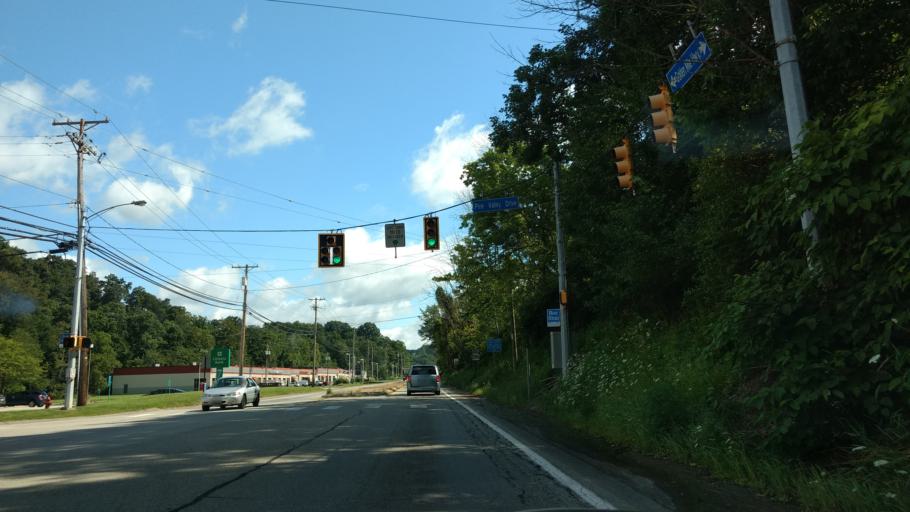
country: US
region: Pennsylvania
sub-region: Westmoreland County
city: Murrysville
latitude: 40.4549
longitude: -79.7109
